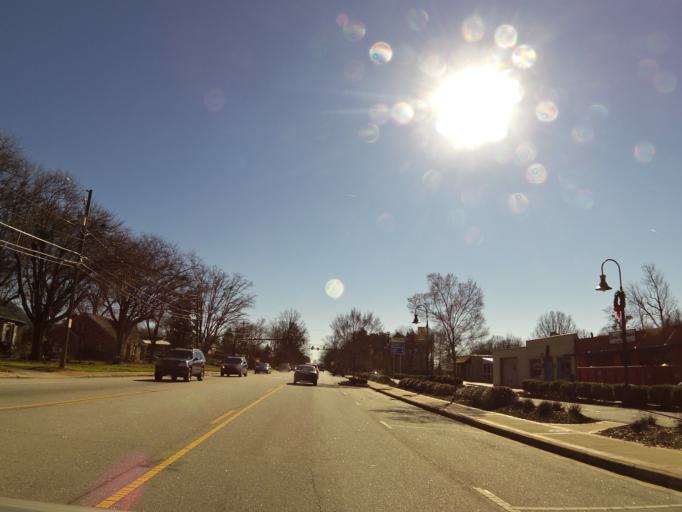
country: US
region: South Carolina
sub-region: Greenville County
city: Travelers Rest
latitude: 34.9617
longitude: -82.4405
